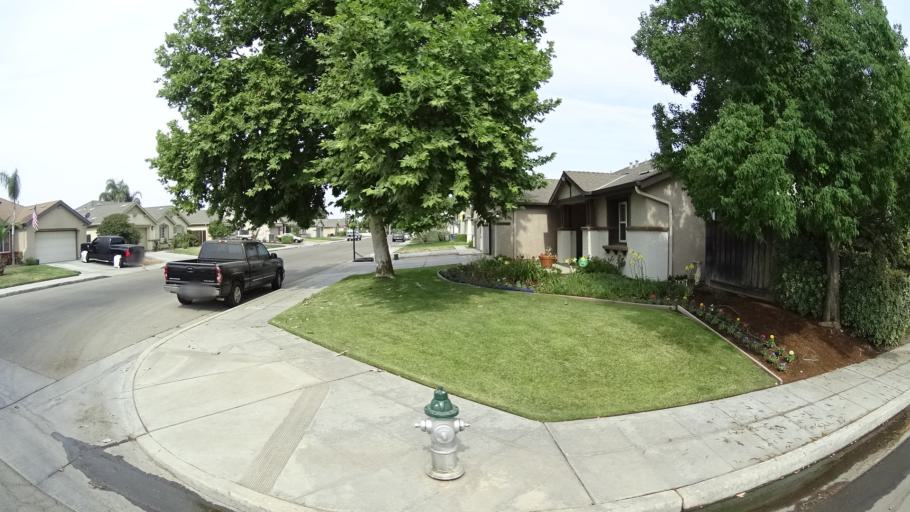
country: US
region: California
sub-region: Fresno County
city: West Park
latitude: 36.7661
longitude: -119.8874
